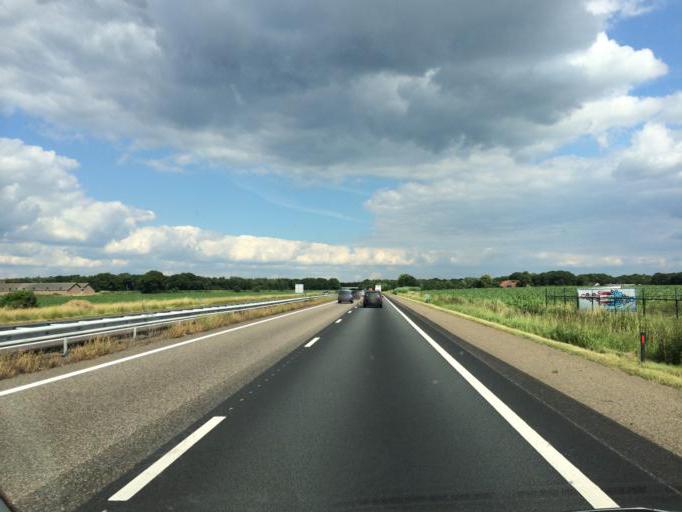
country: NL
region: North Brabant
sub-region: Gemeente Someren
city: Someren
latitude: 51.4208
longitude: 5.7154
